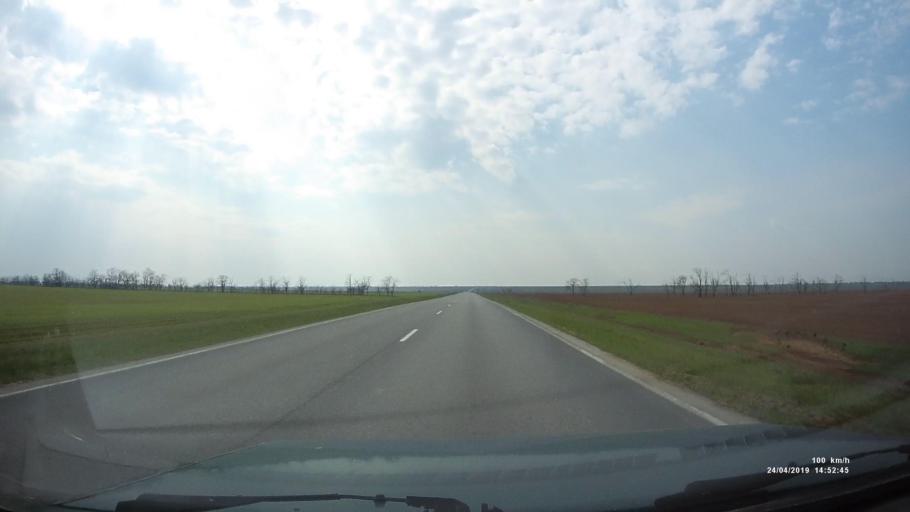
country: RU
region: Rostov
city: Remontnoye
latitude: 46.5307
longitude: 43.6739
